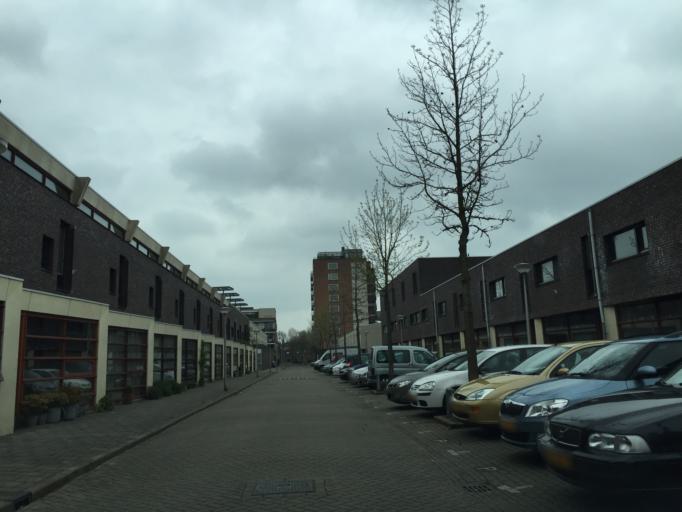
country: NL
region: South Holland
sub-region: Gemeente Delft
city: Delft
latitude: 52.0029
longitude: 4.3593
